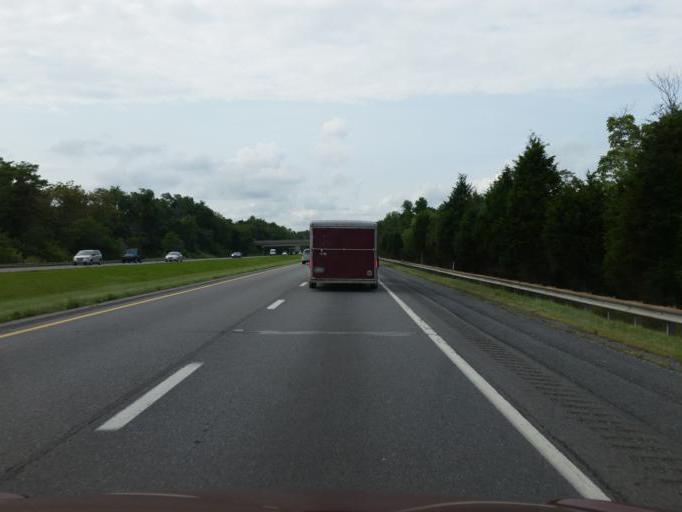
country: US
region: Pennsylvania
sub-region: Dauphin County
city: Middletown
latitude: 40.2108
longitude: -76.7072
